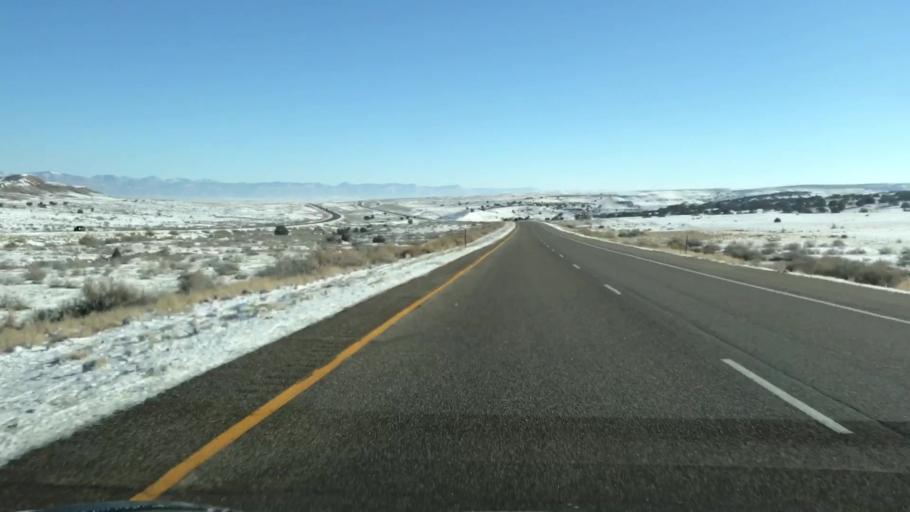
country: US
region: Colorado
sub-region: Mesa County
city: Loma
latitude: 39.2212
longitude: -108.9536
